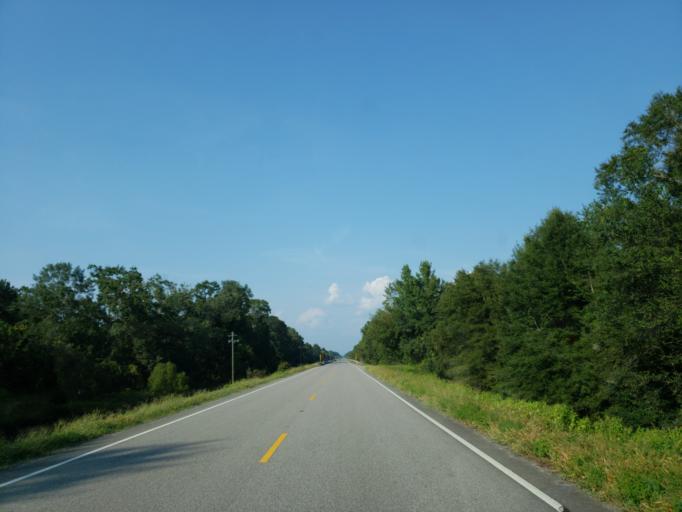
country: US
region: Alabama
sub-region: Sumter County
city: Livingston
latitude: 32.7108
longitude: -88.0806
